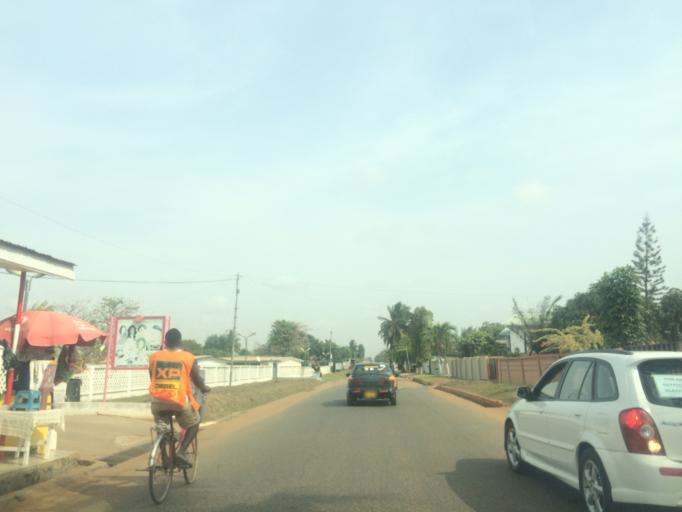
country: GH
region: Greater Accra
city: Nungua
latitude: 5.5987
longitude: -0.0906
